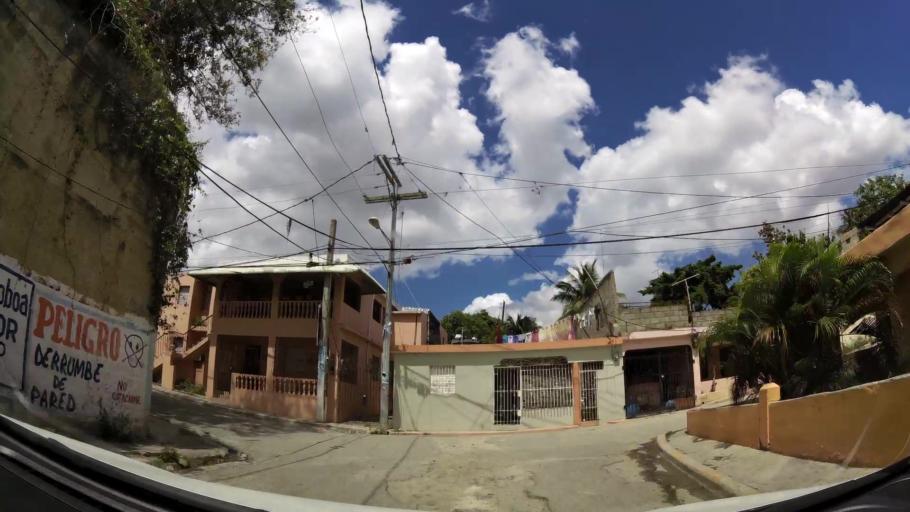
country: DO
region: Nacional
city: Ensanche Luperon
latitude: 18.5226
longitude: -69.9163
